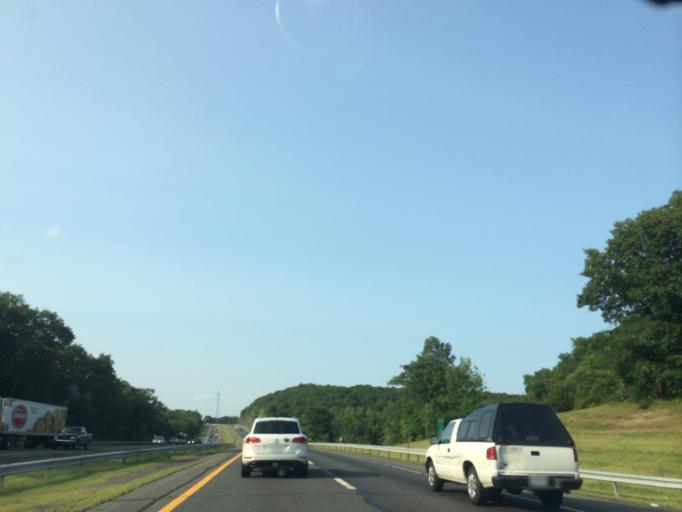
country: US
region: New York
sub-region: Greene County
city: Jefferson Heights
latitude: 42.1876
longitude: -73.9230
